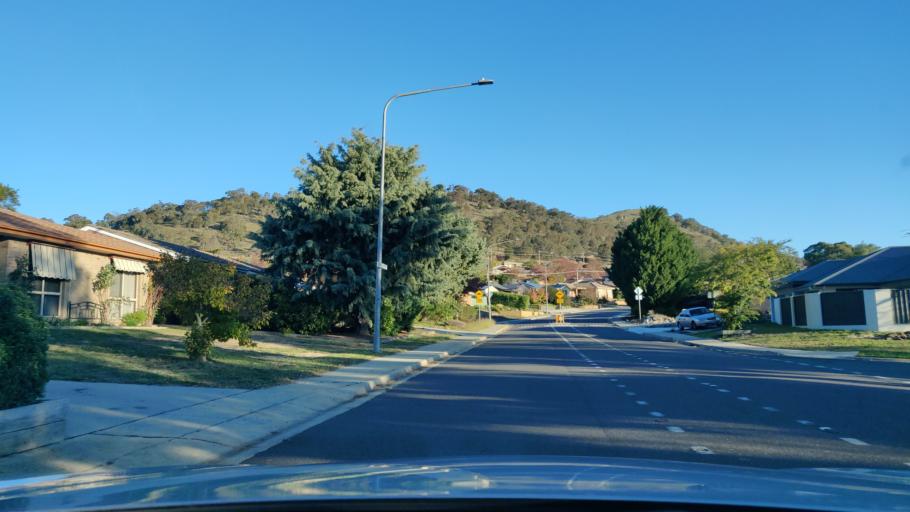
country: AU
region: Australian Capital Territory
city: Macarthur
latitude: -35.4479
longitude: 149.1245
